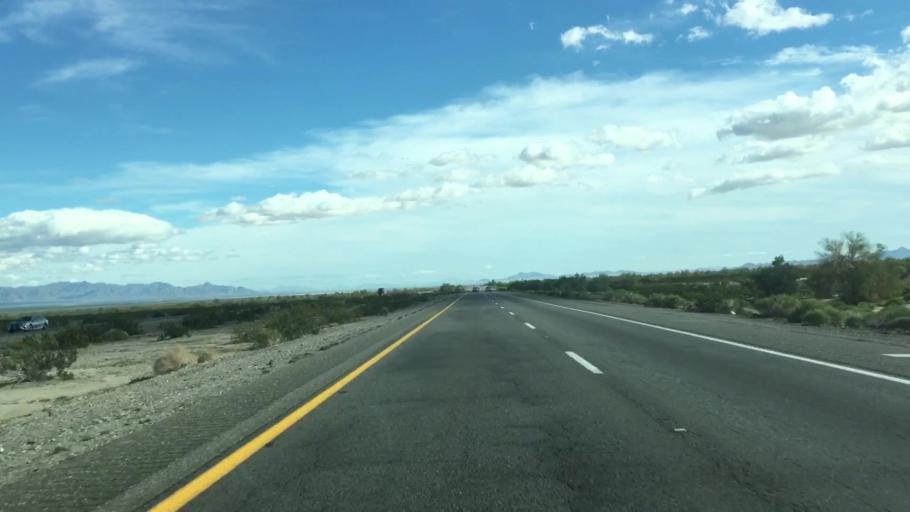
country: US
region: California
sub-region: Riverside County
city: Mesa Verde
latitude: 33.6661
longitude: -115.1887
